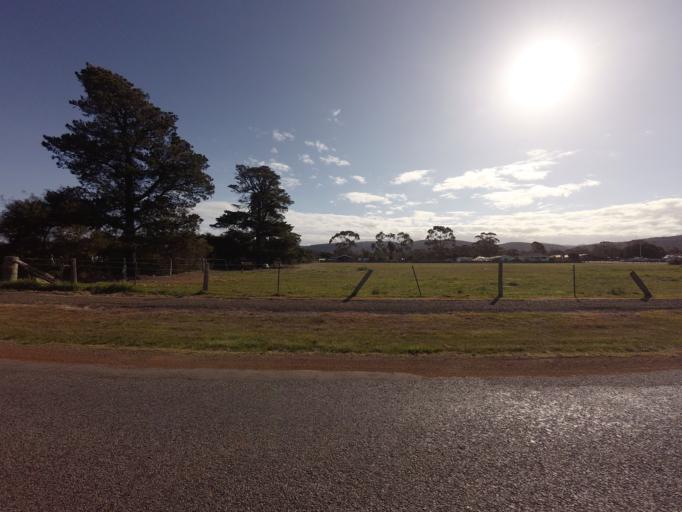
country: AU
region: Tasmania
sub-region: Sorell
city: Sorell
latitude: -42.5027
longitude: 147.9153
